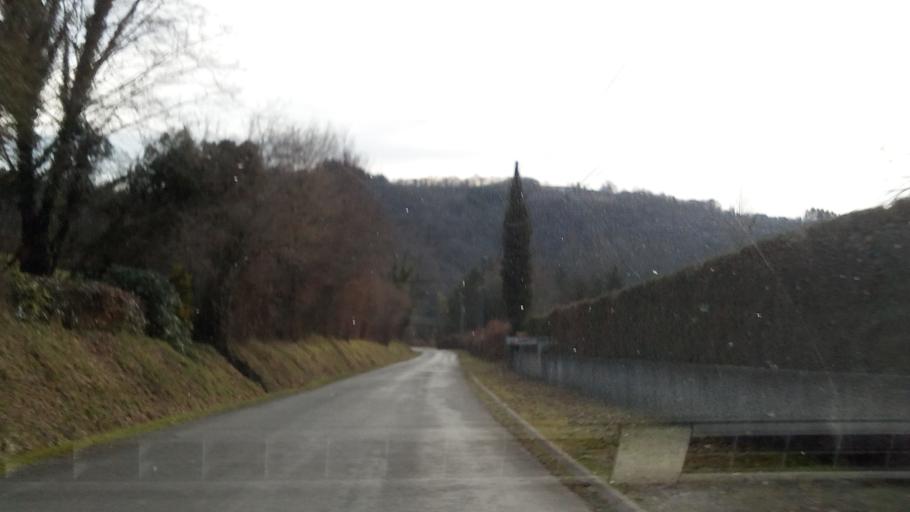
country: FR
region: Limousin
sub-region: Departement de la Correze
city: Naves
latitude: 45.3047
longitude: 1.7973
